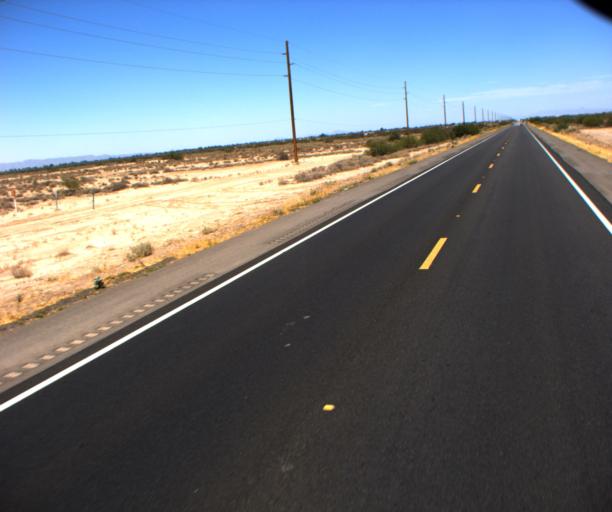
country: US
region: Arizona
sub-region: Maricopa County
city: Sun Lakes
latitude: 33.1740
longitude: -111.8409
